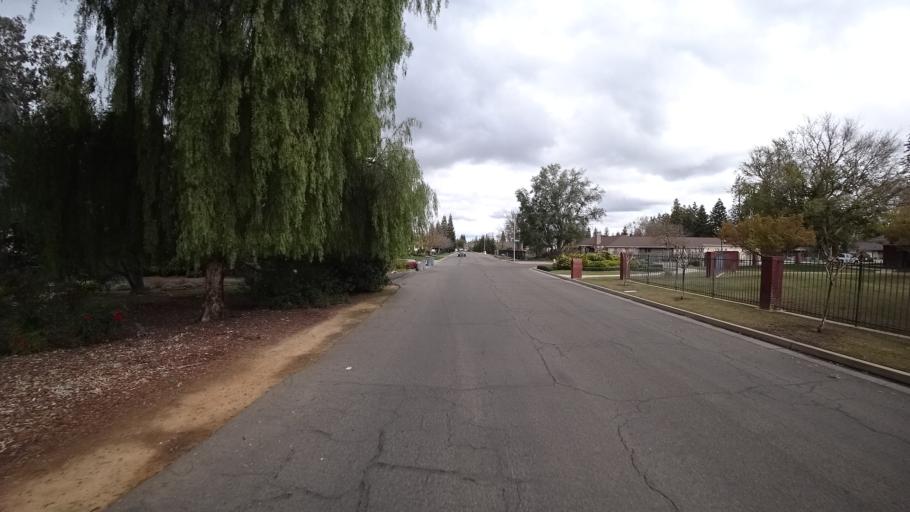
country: US
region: California
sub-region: Fresno County
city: Fresno
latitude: 36.8349
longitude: -119.8308
